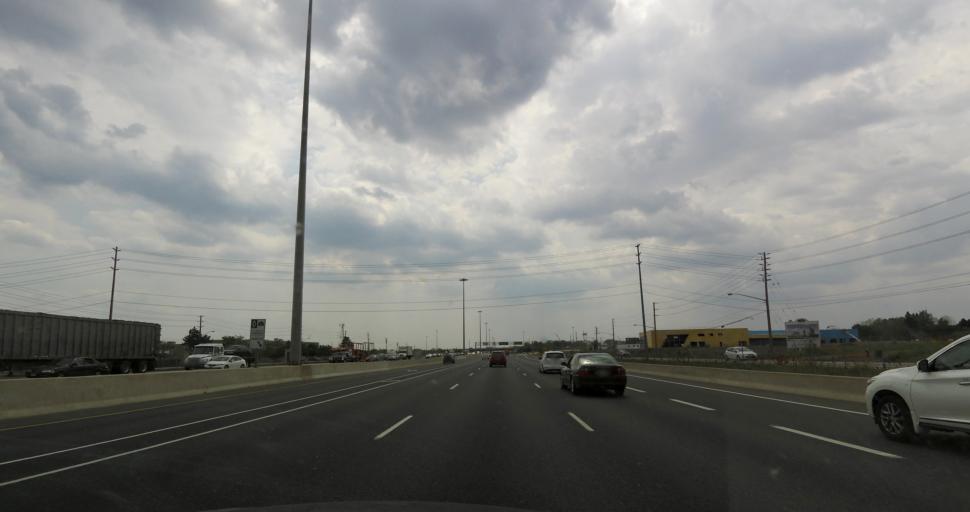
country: CA
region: Ontario
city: Oakville
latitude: 43.4292
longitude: -79.7197
